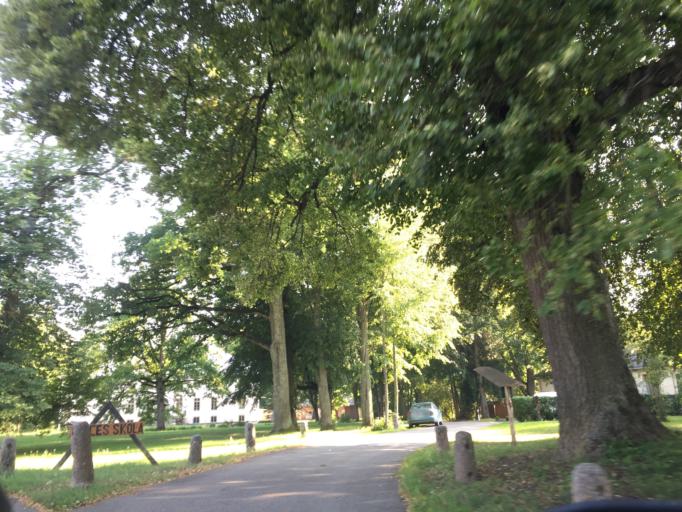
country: LV
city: Tervete
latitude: 56.4218
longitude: 23.5432
